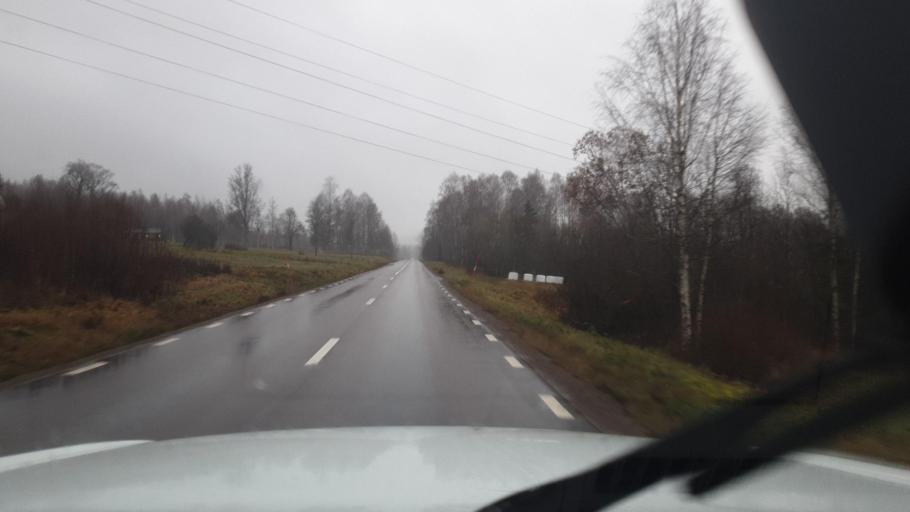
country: SE
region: Vaermland
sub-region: Torsby Kommun
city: Torsby
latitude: 59.9312
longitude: 12.8990
